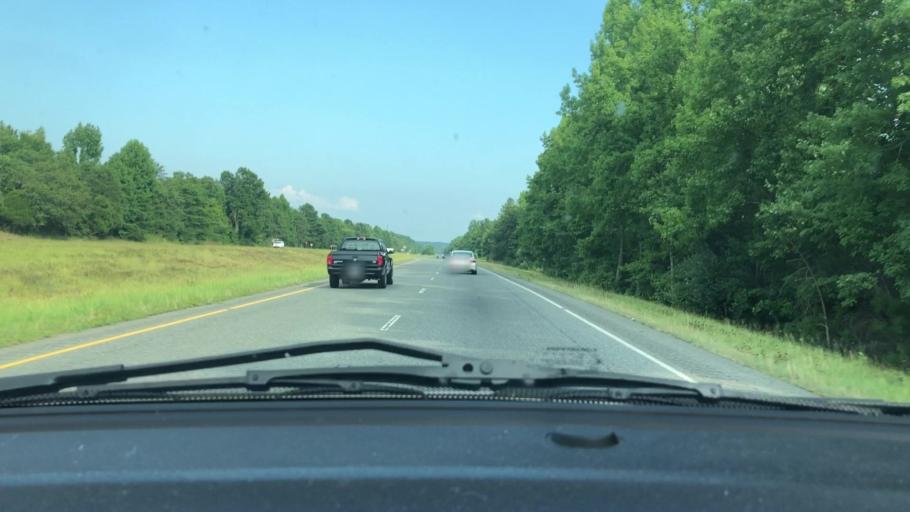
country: US
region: North Carolina
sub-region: Guilford County
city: Forest Oaks
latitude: 35.9006
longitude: -79.6663
